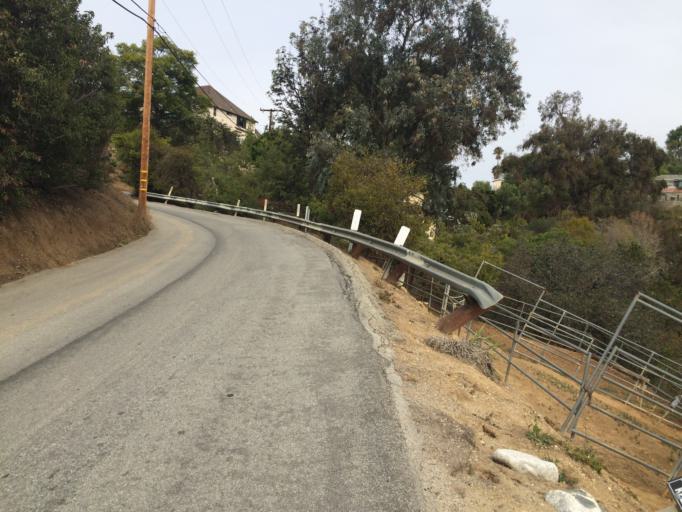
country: US
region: California
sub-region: Los Angeles County
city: La Habra Heights
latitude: 33.9557
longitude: -117.9379
